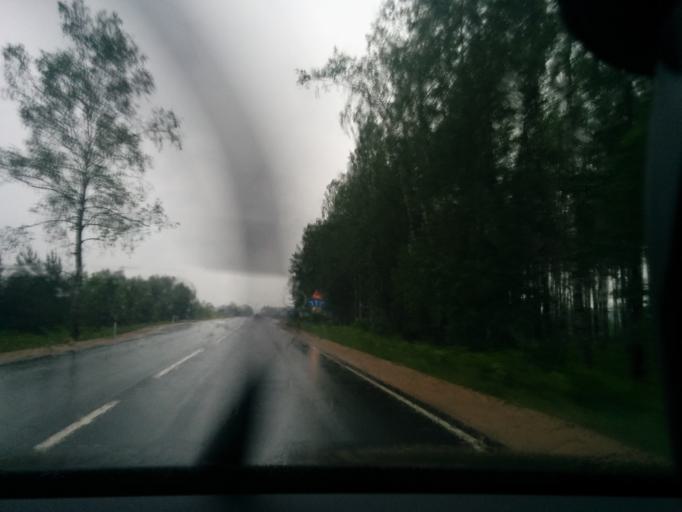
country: LV
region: Ikskile
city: Ikskile
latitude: 56.8863
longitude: 24.4921
